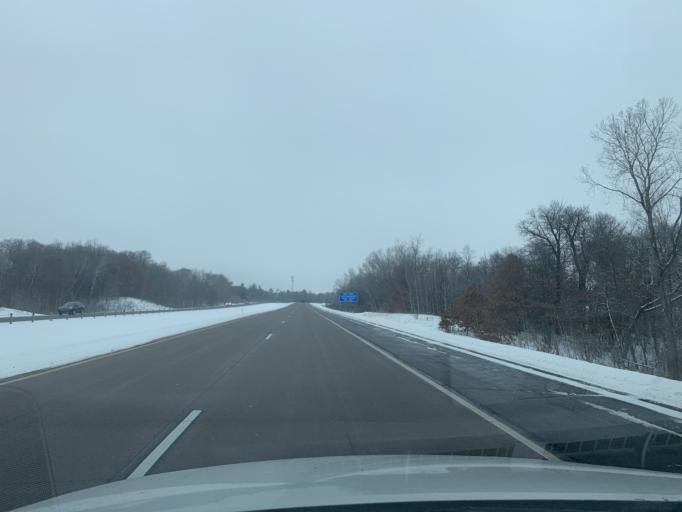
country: US
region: Minnesota
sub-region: Chisago County
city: Harris
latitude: 45.5873
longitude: -92.9939
